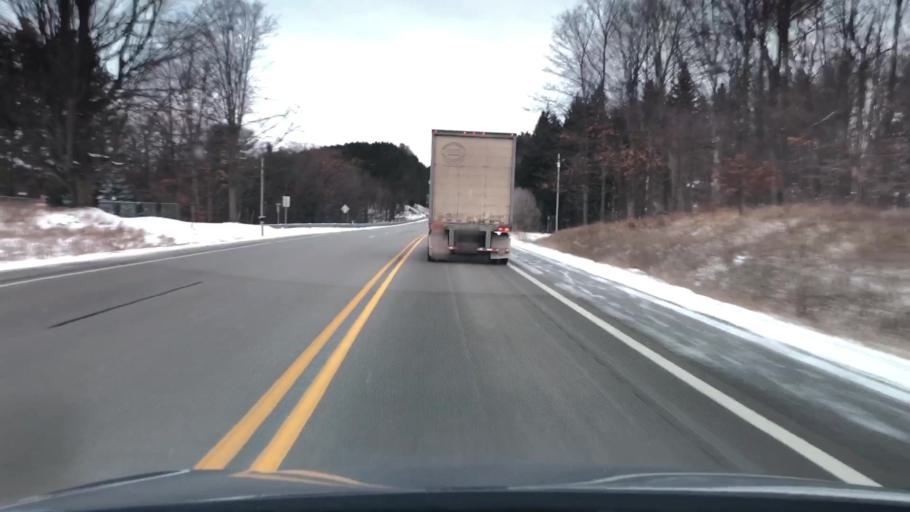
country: US
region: Michigan
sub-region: Wexford County
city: Cadillac
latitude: 44.1790
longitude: -85.3795
